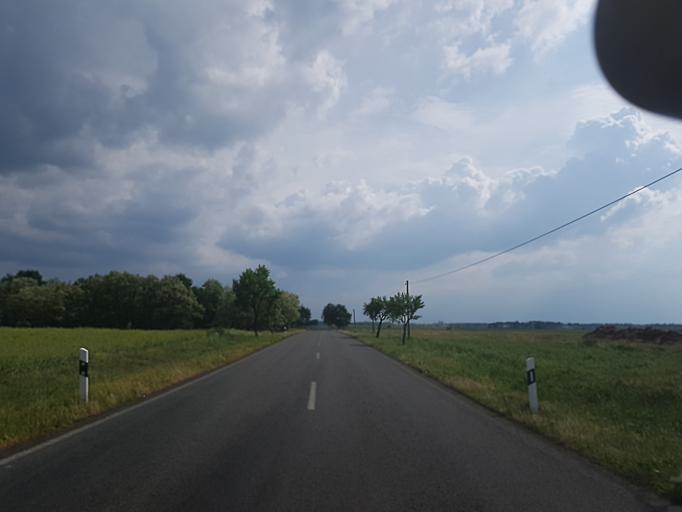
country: DE
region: Saxony-Anhalt
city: Rodleben
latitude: 52.0060
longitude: 12.2339
